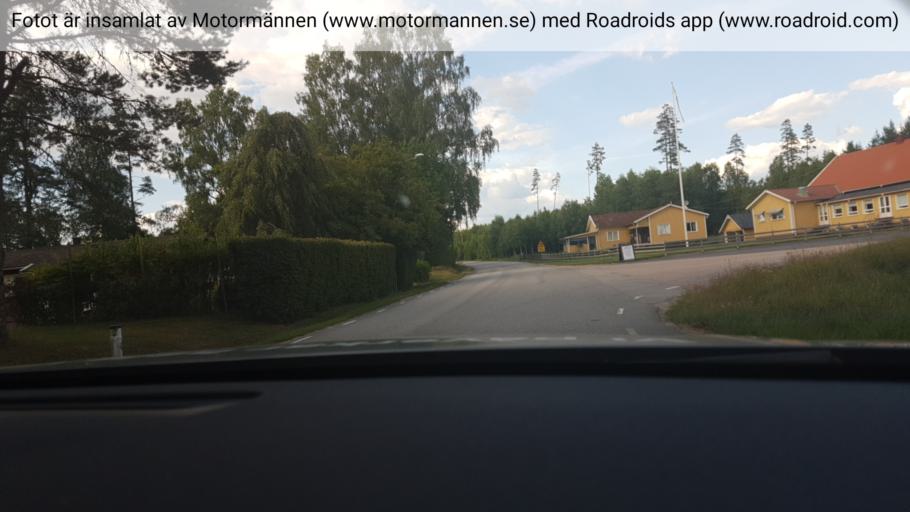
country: SE
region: Vaestra Goetaland
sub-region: Svenljunga Kommun
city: Svenljunga
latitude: 57.4383
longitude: 13.1419
